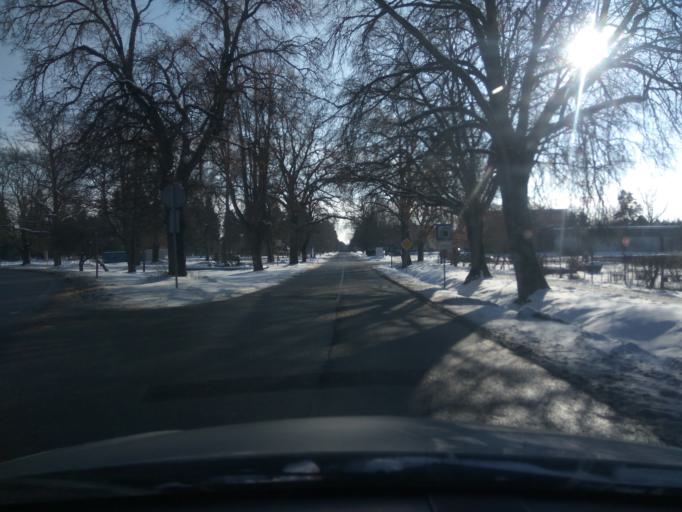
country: LV
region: Kuldigas Rajons
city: Kuldiga
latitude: 57.2776
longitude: 22.0216
